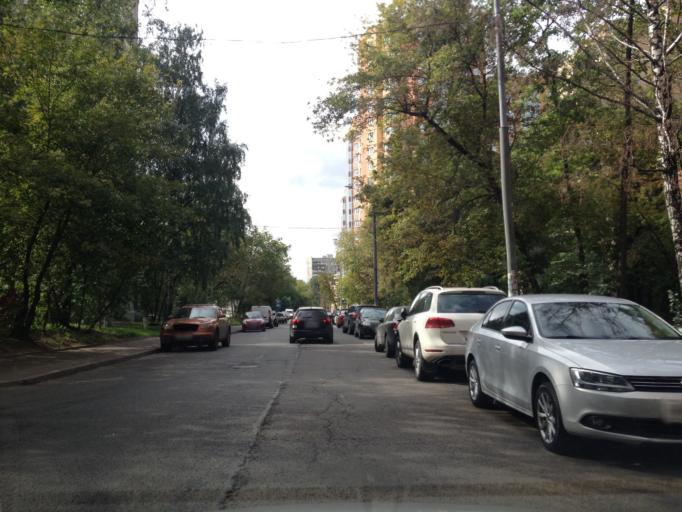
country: RU
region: Moskovskaya
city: Izmaylovo
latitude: 55.7900
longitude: 37.7901
